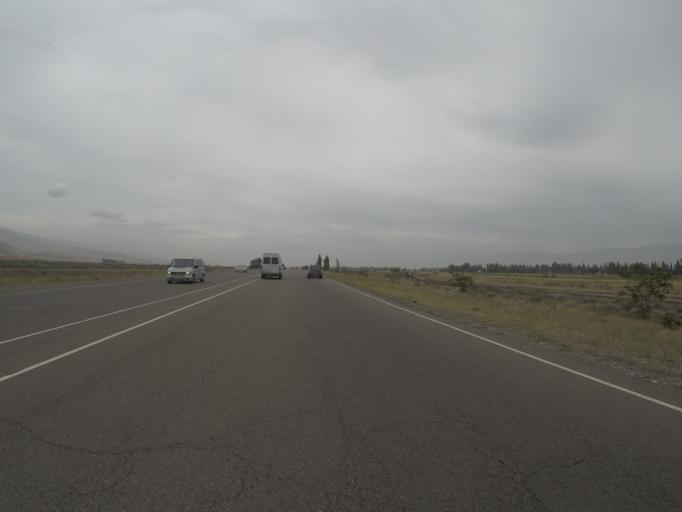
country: KG
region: Chuy
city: Bystrovka
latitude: 42.8290
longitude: 75.5294
